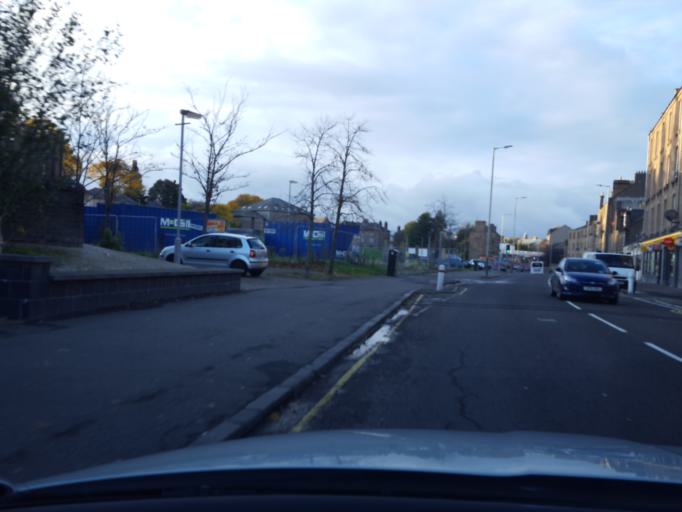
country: GB
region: Scotland
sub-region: Dundee City
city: Dundee
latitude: 56.4719
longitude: -2.9767
